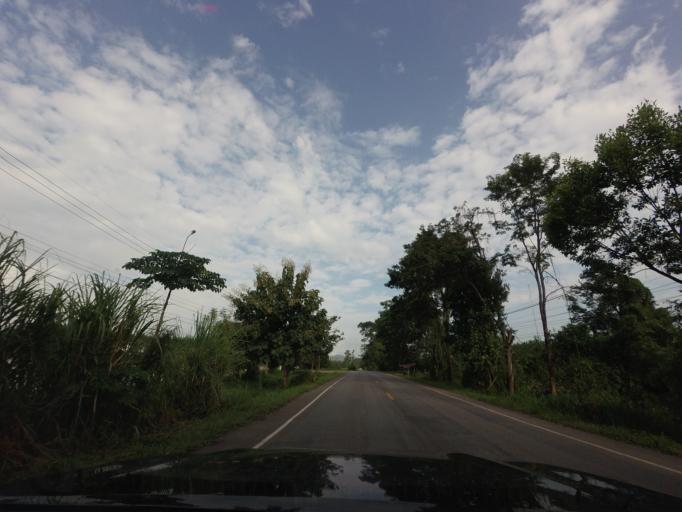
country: TH
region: Nong Khai
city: Pho Tak
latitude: 17.7913
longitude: 102.3591
